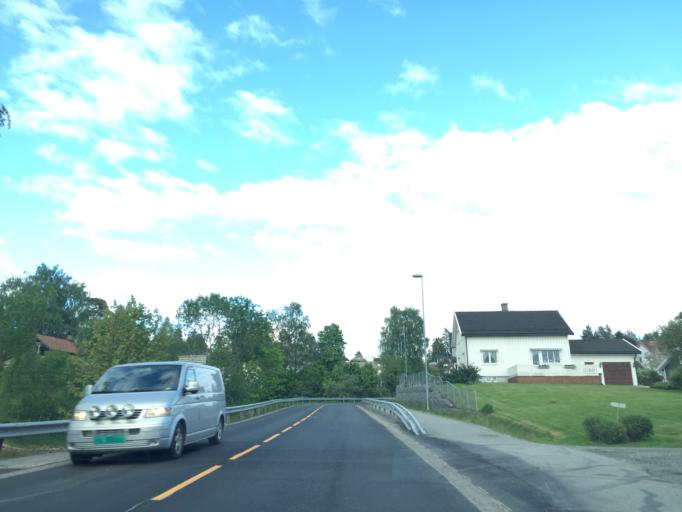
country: NO
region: Akershus
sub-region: Fet
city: Fetsund
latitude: 59.9323
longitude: 11.1848
